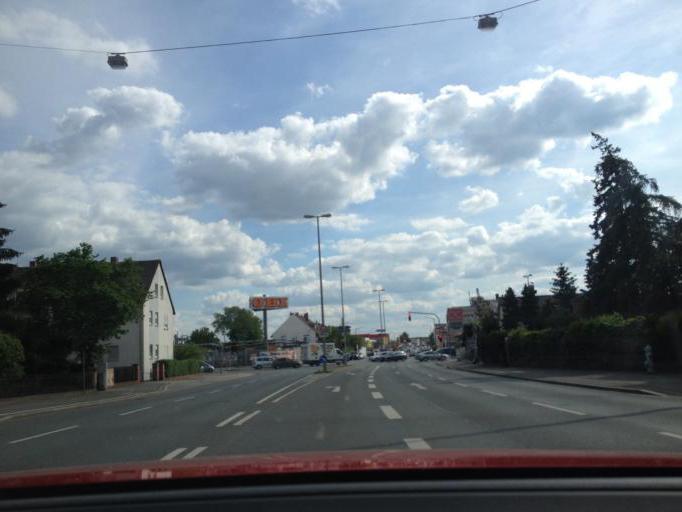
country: DE
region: Bavaria
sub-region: Regierungsbezirk Mittelfranken
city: Grossreuth bei Schweinau
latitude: 49.4545
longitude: 11.0165
